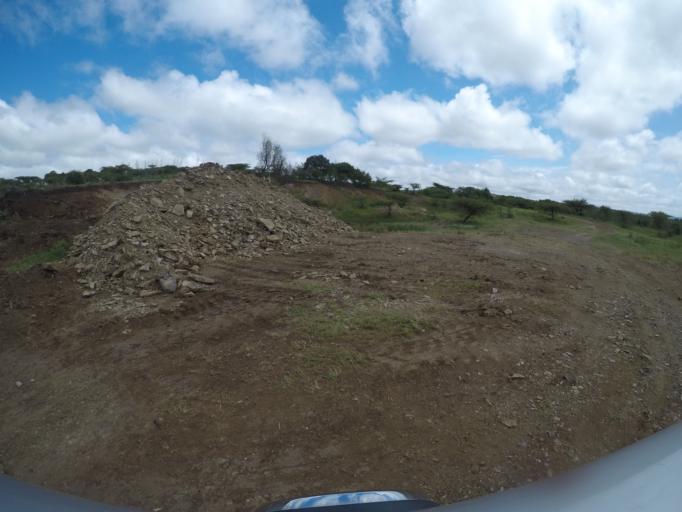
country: ZA
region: KwaZulu-Natal
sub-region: uThungulu District Municipality
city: Empangeni
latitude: -28.5732
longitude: 31.8371
